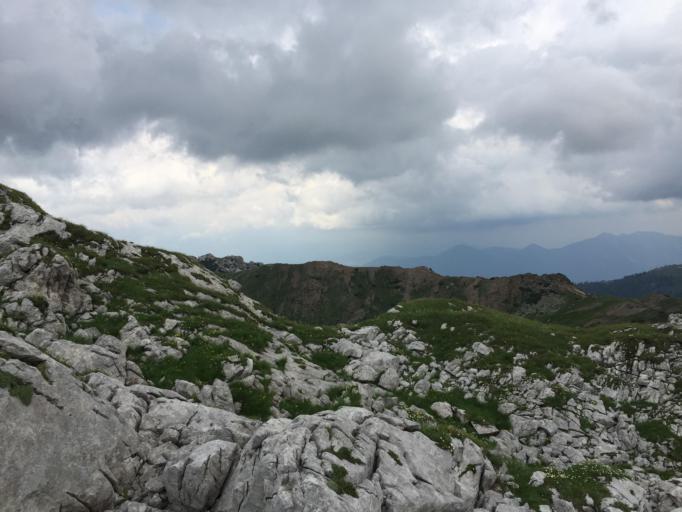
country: IT
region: Friuli Venezia Giulia
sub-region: Provincia di Udine
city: Pontebba
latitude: 46.5553
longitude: 13.2266
